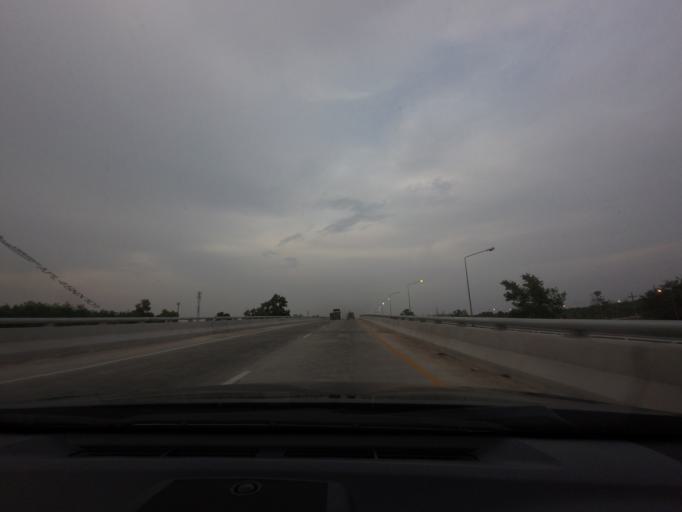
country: TH
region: Surat Thani
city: Phunphin
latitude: 9.1533
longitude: 99.1620
